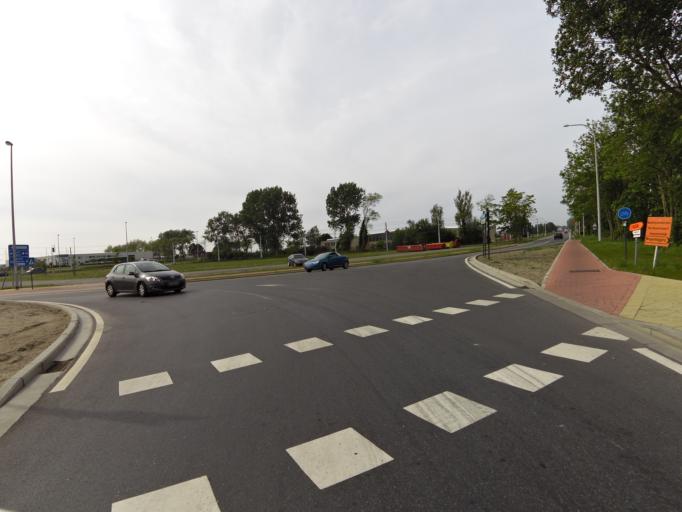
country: BE
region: Flanders
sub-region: Provincie West-Vlaanderen
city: Nieuwpoort
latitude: 51.1373
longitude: 2.7556
